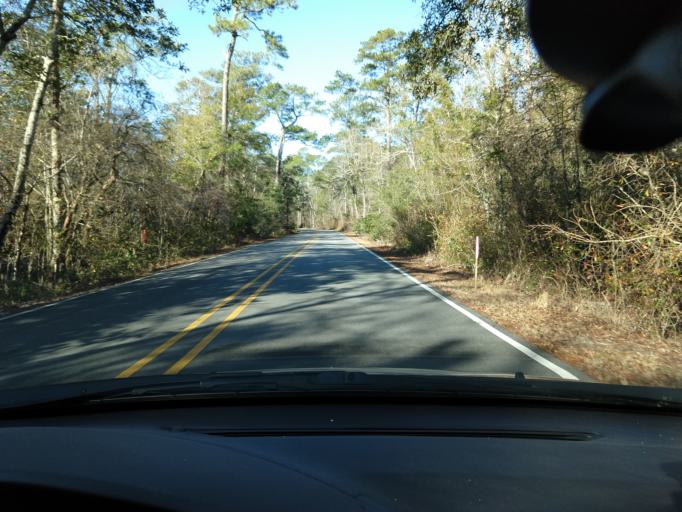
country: US
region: Mississippi
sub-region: Jackson County
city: Gulf Park Estates
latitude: 30.3961
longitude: -88.7840
